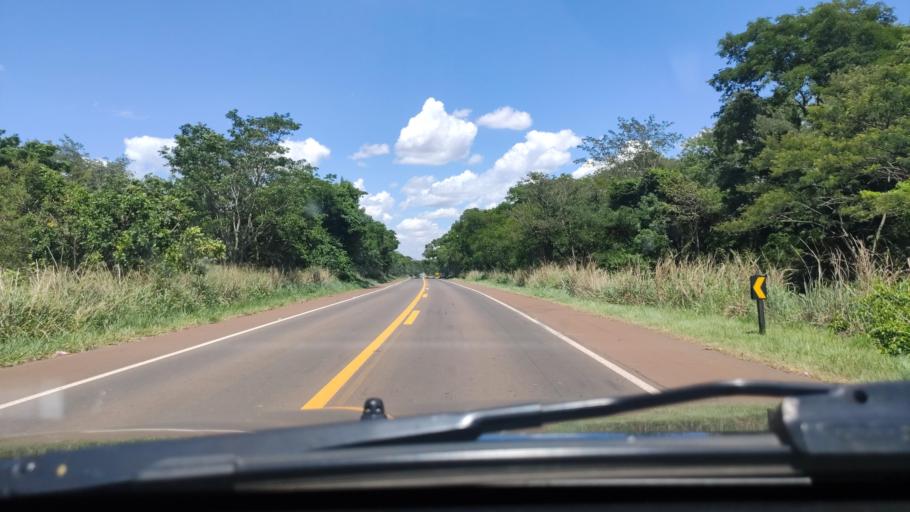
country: BR
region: Sao Paulo
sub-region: Boa Esperanca Do Sul
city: Boa Esperanca do Sul
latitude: -22.0690
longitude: -48.3697
